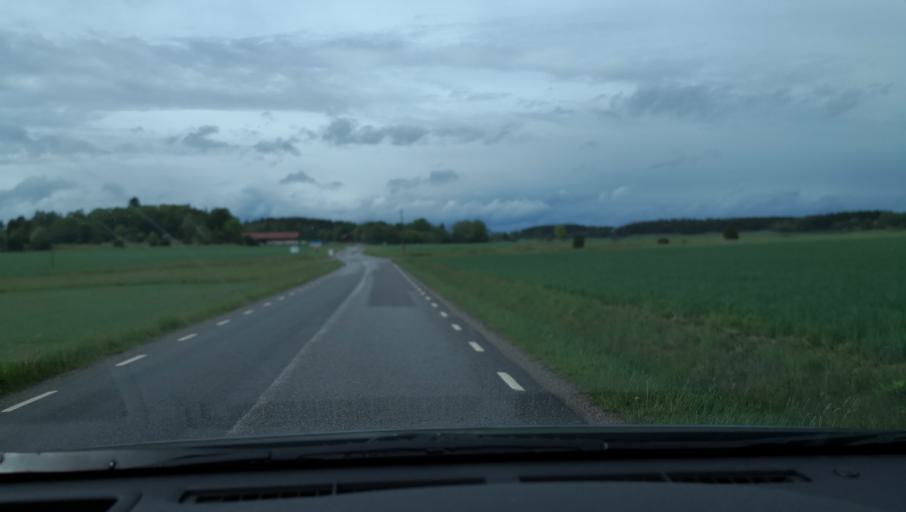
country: SE
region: Uppsala
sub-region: Enkopings Kommun
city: Orsundsbro
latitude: 59.7038
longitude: 17.3606
